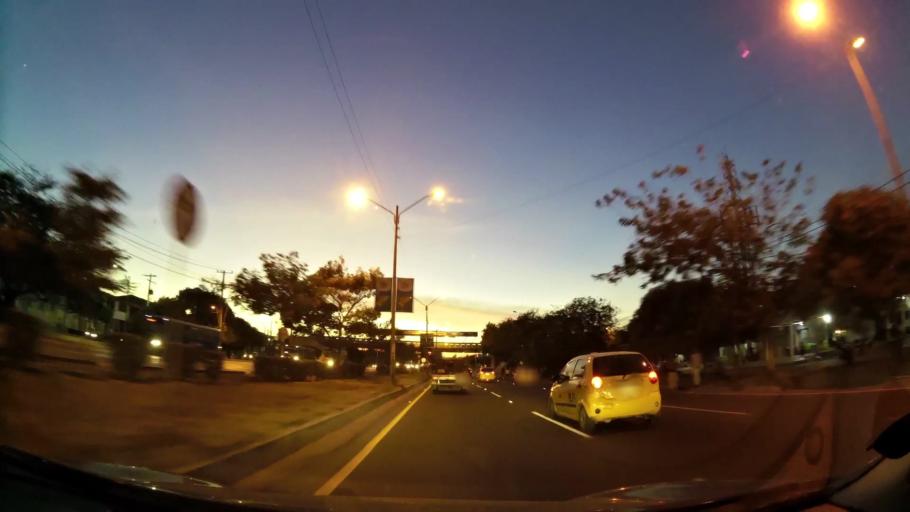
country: CO
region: Atlantico
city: Soledad
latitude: 10.9231
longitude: -74.8060
